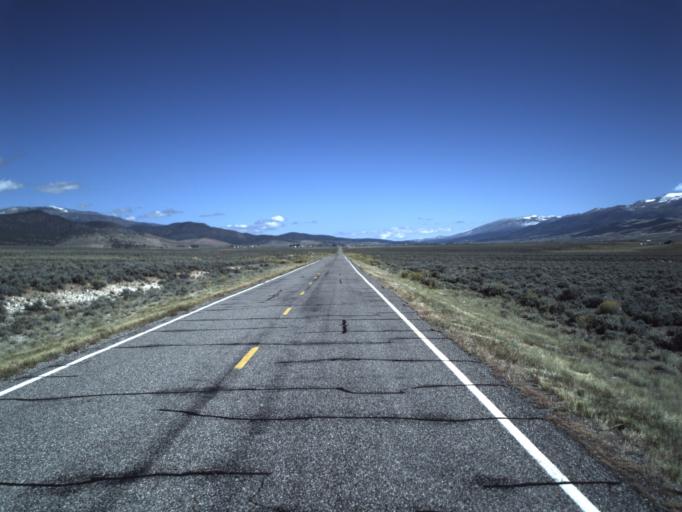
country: US
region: Utah
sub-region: Wayne County
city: Loa
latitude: 38.3809
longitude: -111.9358
